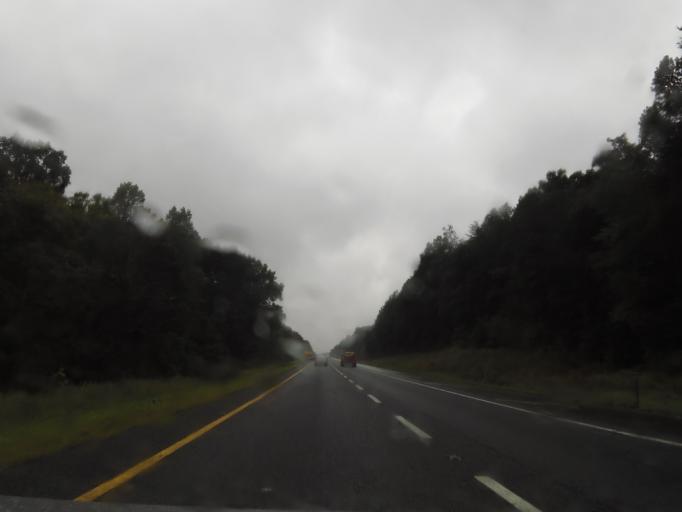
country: US
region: Tennessee
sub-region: Bradley County
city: Hopewell
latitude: 35.2706
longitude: -84.8264
